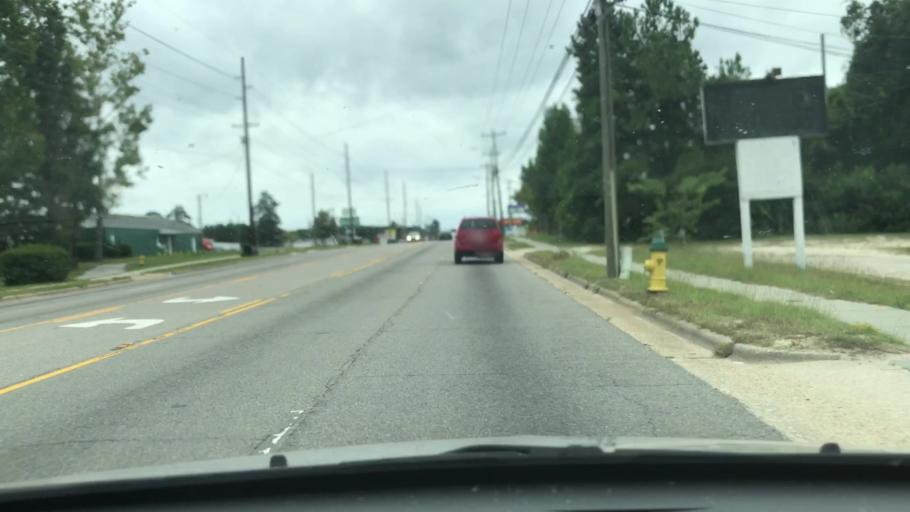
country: US
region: North Carolina
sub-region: Cumberland County
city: Fayetteville
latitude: 35.1010
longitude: -78.9190
